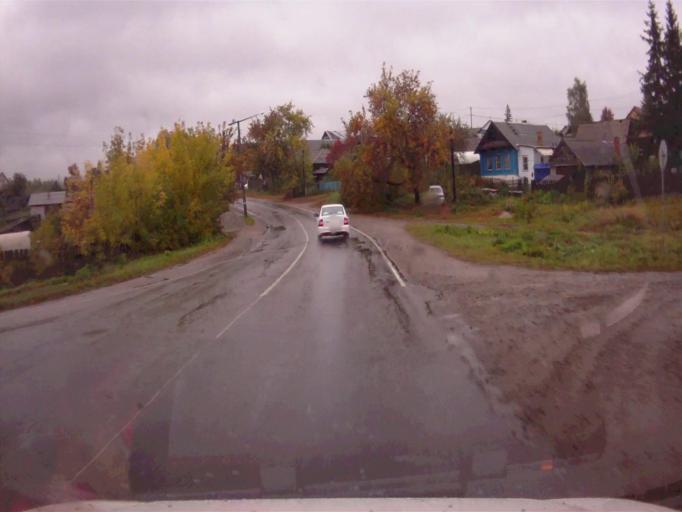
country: RU
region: Chelyabinsk
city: Kyshtym
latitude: 55.7234
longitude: 60.5267
